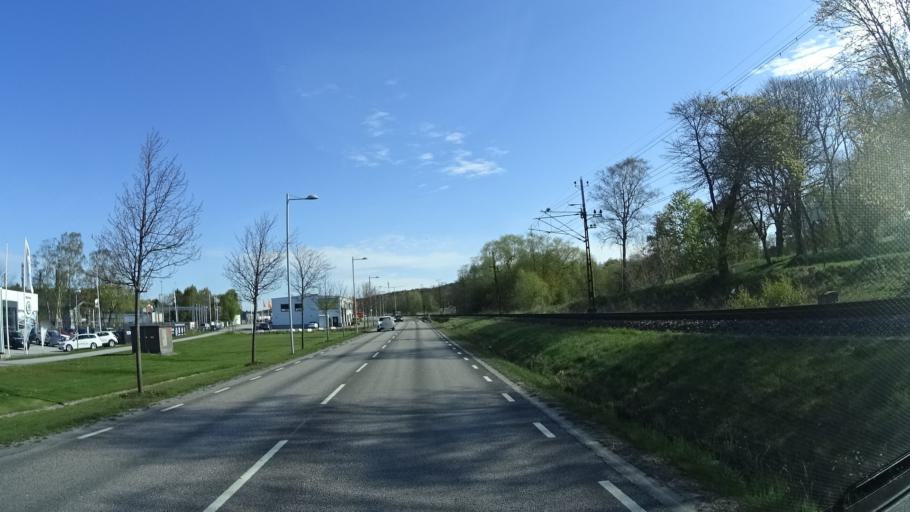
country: SE
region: Vaestra Goetaland
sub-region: Stenungsunds Kommun
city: Stenungsund
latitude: 58.0755
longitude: 11.8273
